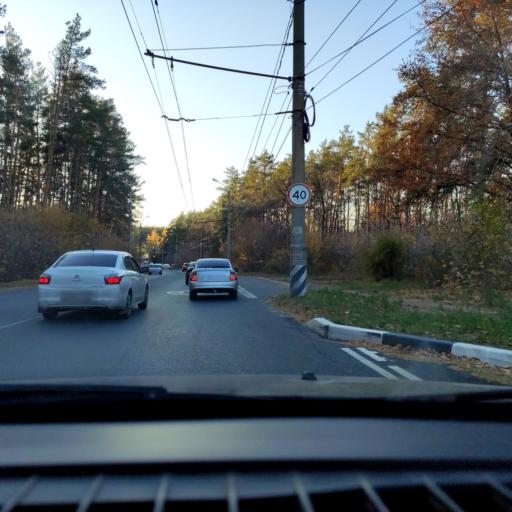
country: RU
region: Samara
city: Tol'yatti
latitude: 53.4784
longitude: 49.3573
